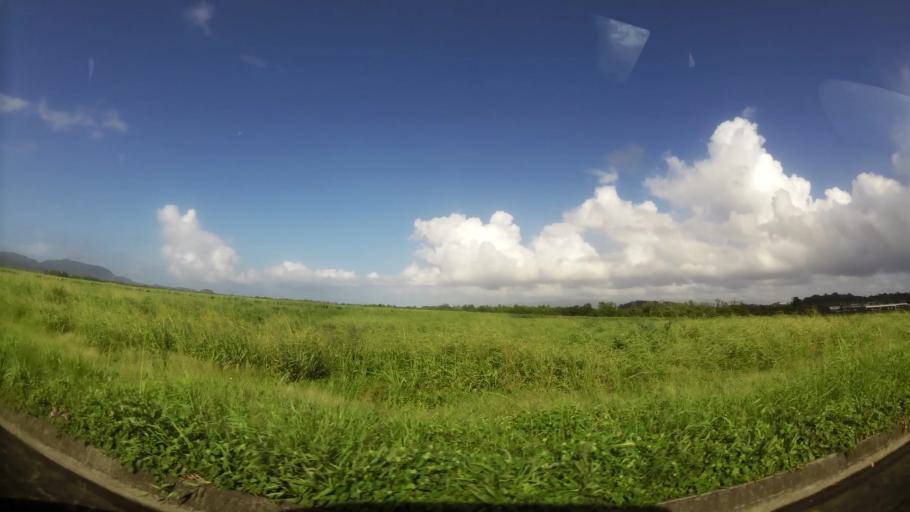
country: MQ
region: Martinique
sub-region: Martinique
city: Ducos
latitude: 14.5487
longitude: -60.9731
